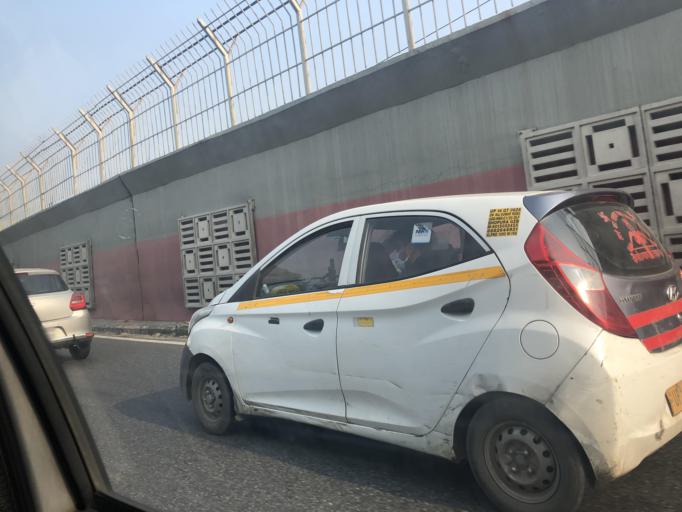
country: IN
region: NCT
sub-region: Central Delhi
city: Karol Bagh
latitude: 28.6130
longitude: 77.1367
